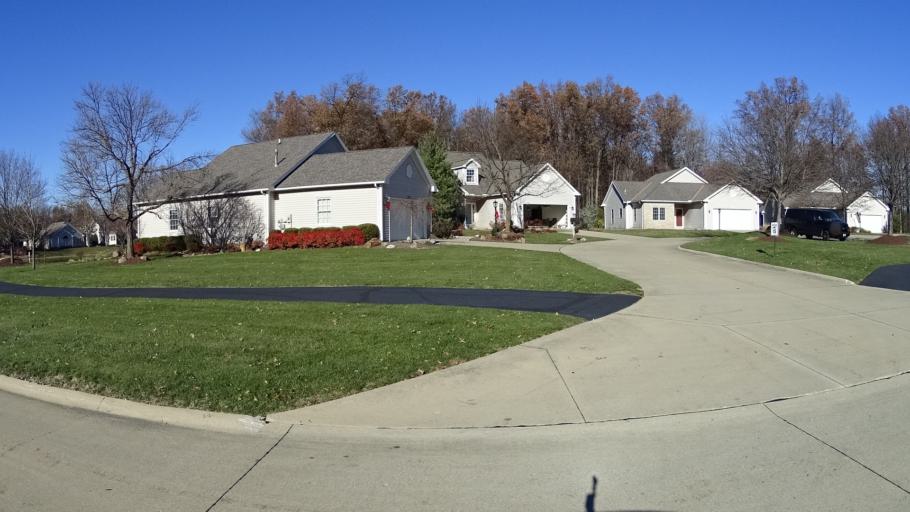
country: US
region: Ohio
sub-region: Lorain County
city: Avon Center
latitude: 41.4291
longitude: -81.9943
